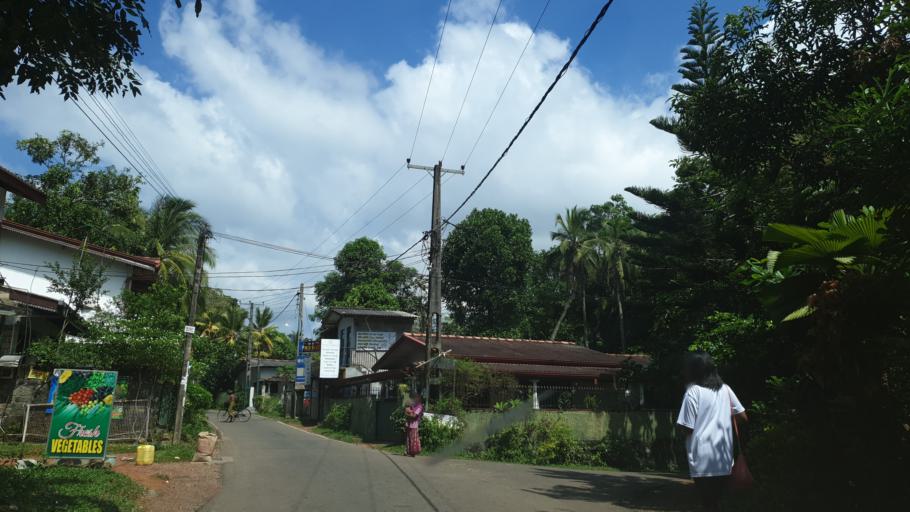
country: LK
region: Western
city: Panadura
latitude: 6.6746
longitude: 79.9396
